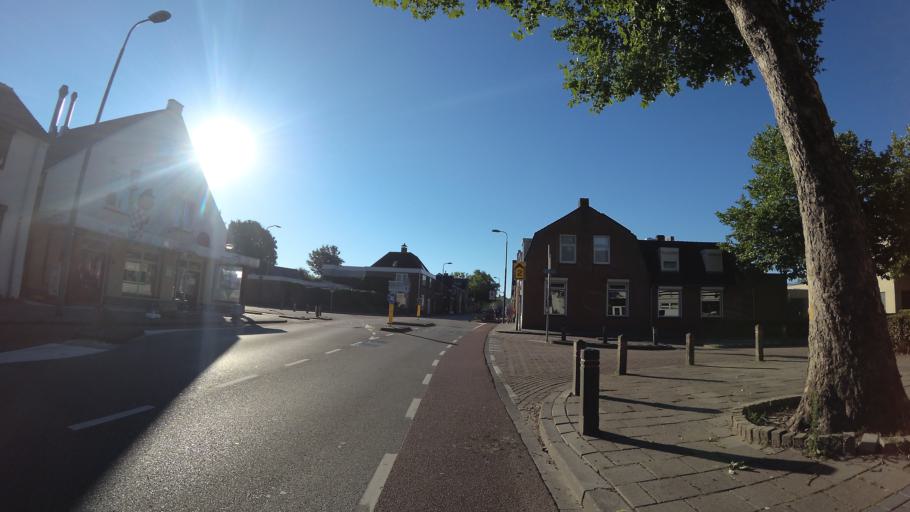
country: NL
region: North Brabant
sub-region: Gemeente Waalwijk
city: Waalwijk
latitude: 51.6568
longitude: 5.0413
